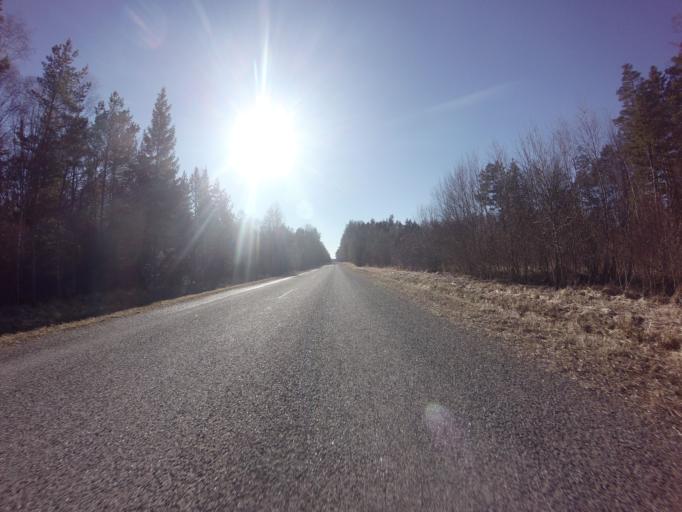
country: EE
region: Saare
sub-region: Kuressaare linn
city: Kuressaare
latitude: 58.4797
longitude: 22.2584
